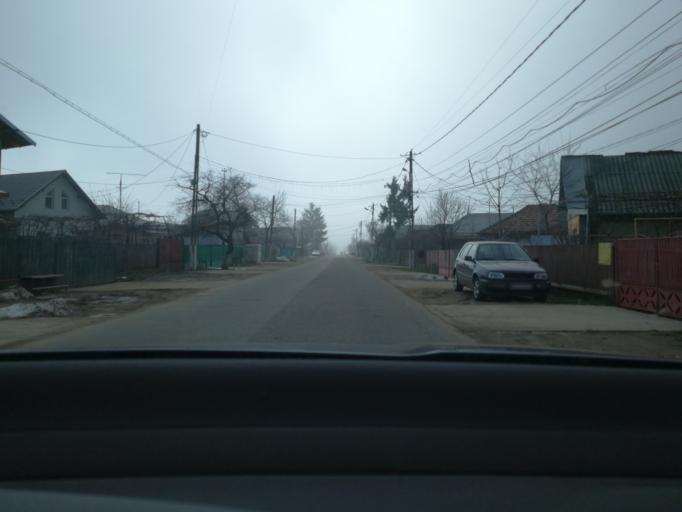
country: RO
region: Prahova
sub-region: Comuna Magureni
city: Lunca Prahovei
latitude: 45.0345
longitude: 25.7628
